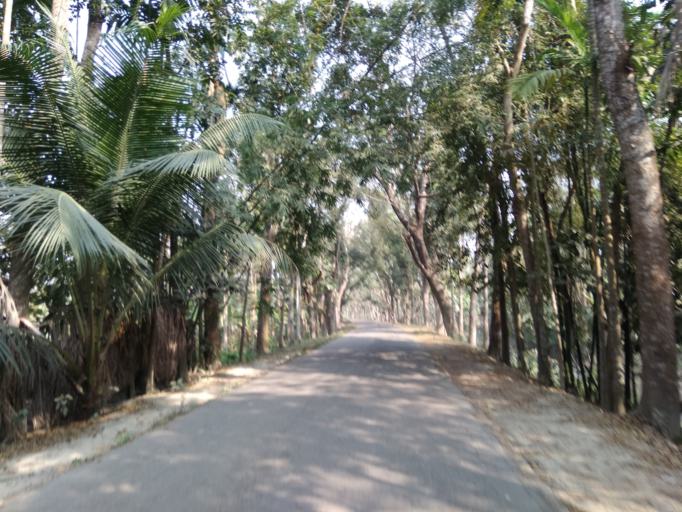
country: BD
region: Barisal
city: Mehendiganj
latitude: 22.9595
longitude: 90.4150
